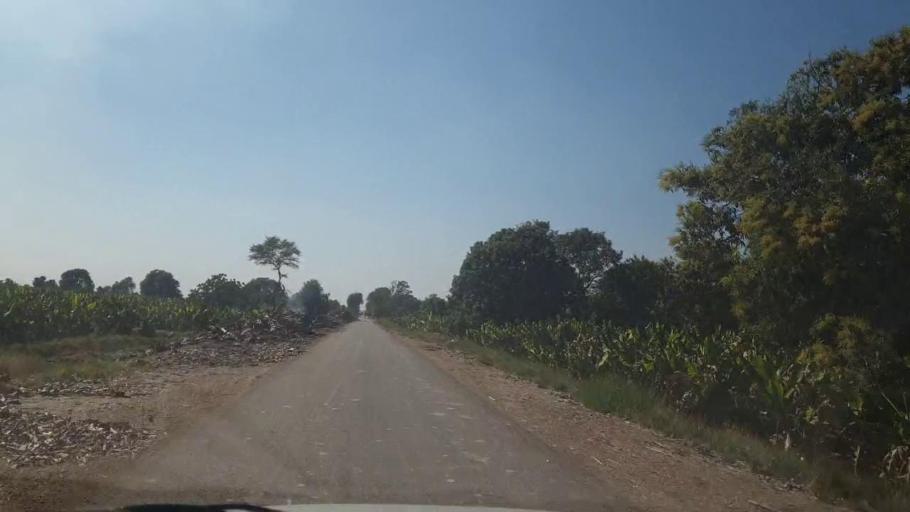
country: PK
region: Sindh
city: Mirpur Khas
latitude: 25.4600
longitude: 69.1800
